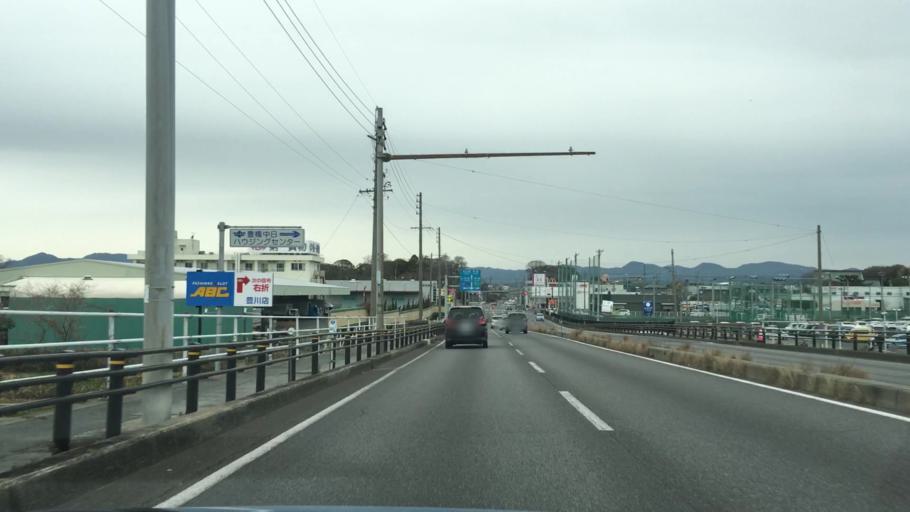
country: JP
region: Aichi
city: Kozakai-cho
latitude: 34.7943
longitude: 137.3697
